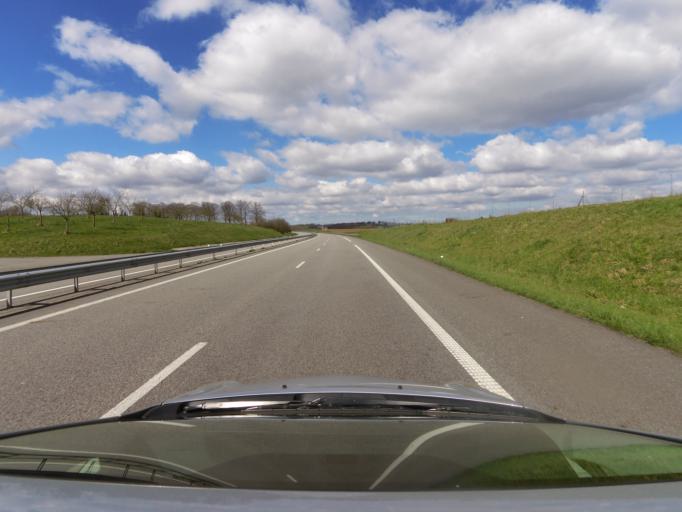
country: FR
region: Haute-Normandie
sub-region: Departement de la Seine-Maritime
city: Limesy
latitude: 49.6571
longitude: 0.9477
